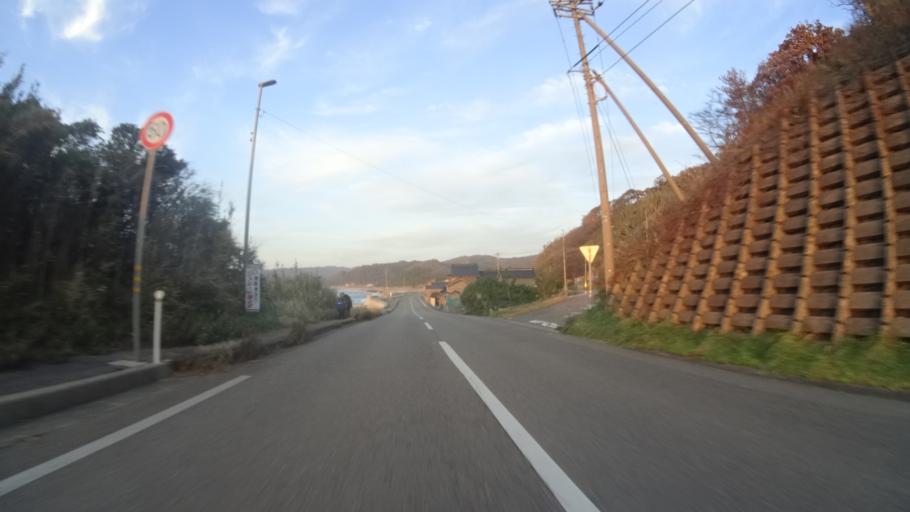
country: JP
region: Ishikawa
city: Nanao
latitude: 37.2535
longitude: 136.7184
